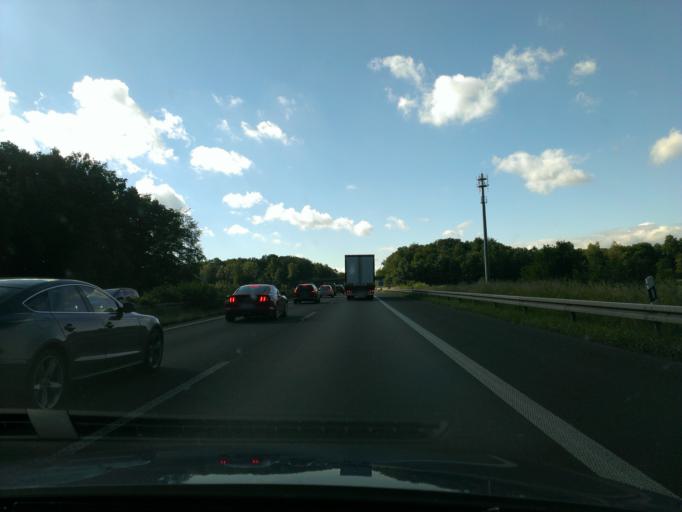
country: DE
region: North Rhine-Westphalia
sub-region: Regierungsbezirk Munster
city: Ascheberg
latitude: 51.8238
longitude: 7.6074
